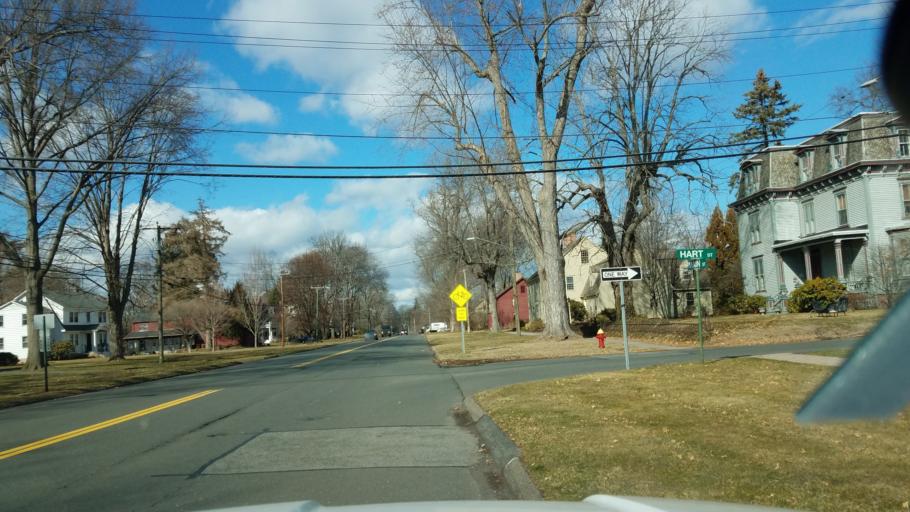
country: US
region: Connecticut
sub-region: Hartford County
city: Wethersfield
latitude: 41.7153
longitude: -72.6526
